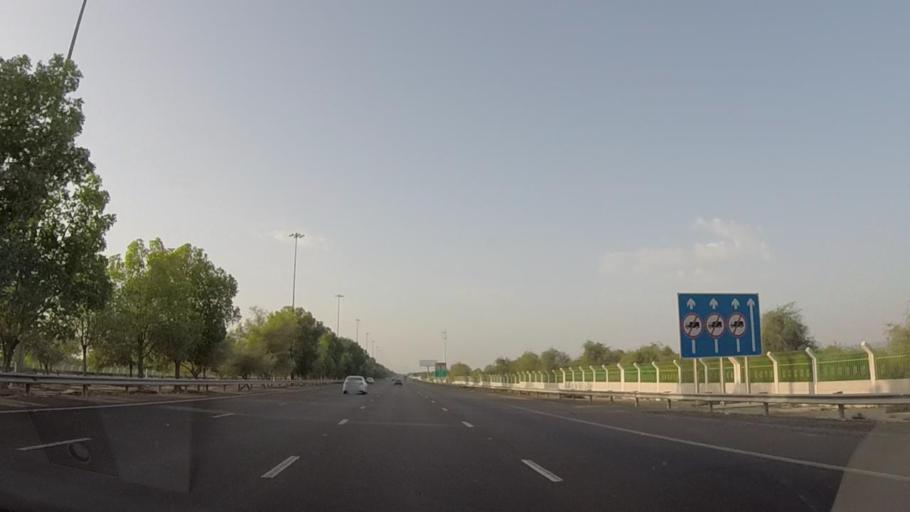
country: AE
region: Dubai
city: Dubai
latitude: 24.7868
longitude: 54.8572
